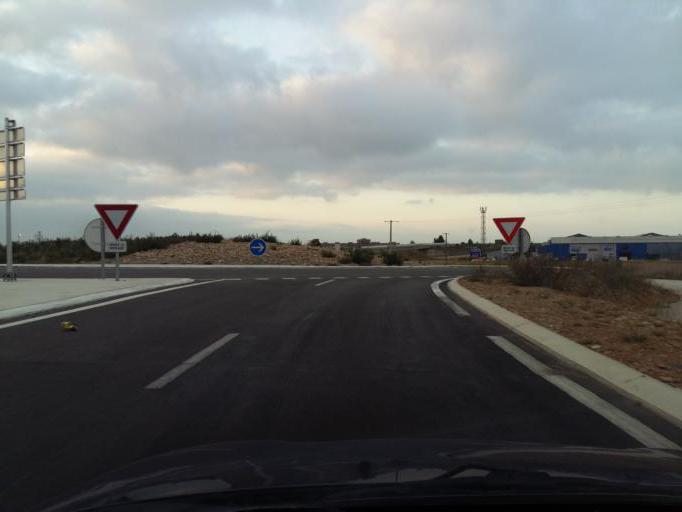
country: FR
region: Provence-Alpes-Cote d'Azur
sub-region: Departement des Bouches-du-Rhone
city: Miramas
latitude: 43.5887
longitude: 4.9894
